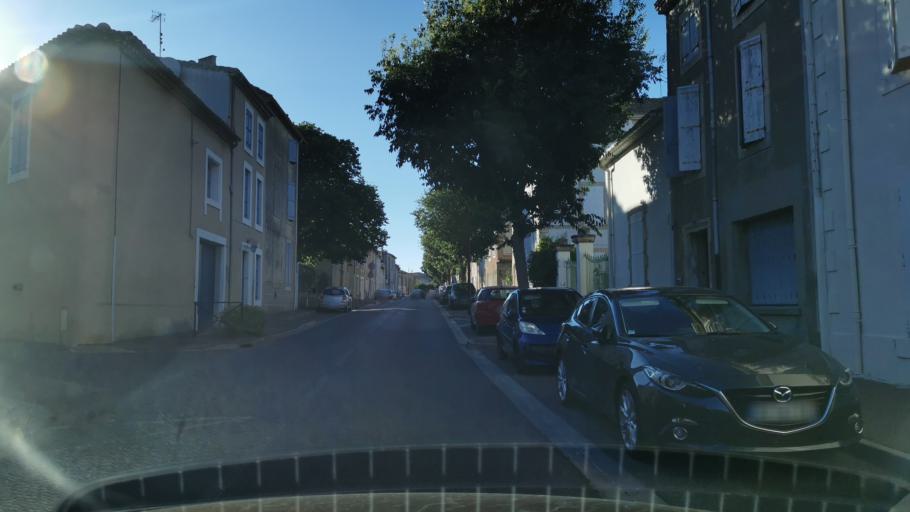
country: FR
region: Languedoc-Roussillon
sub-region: Departement de l'Aude
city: Ouveillan
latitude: 43.2874
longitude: 2.9736
